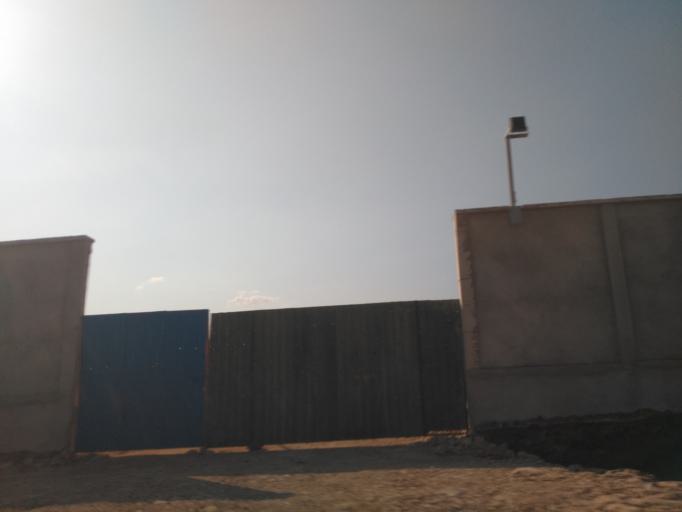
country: TZ
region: Dar es Salaam
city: Dar es Salaam
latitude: -6.8457
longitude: 39.3175
